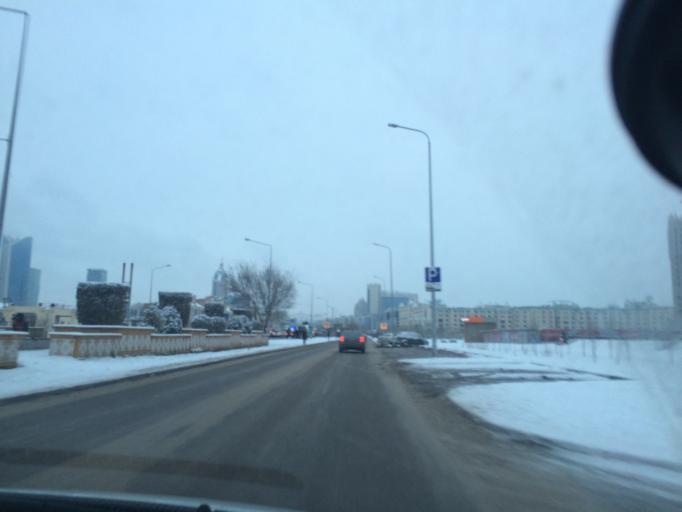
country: KZ
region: Astana Qalasy
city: Astana
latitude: 51.1416
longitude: 71.4186
